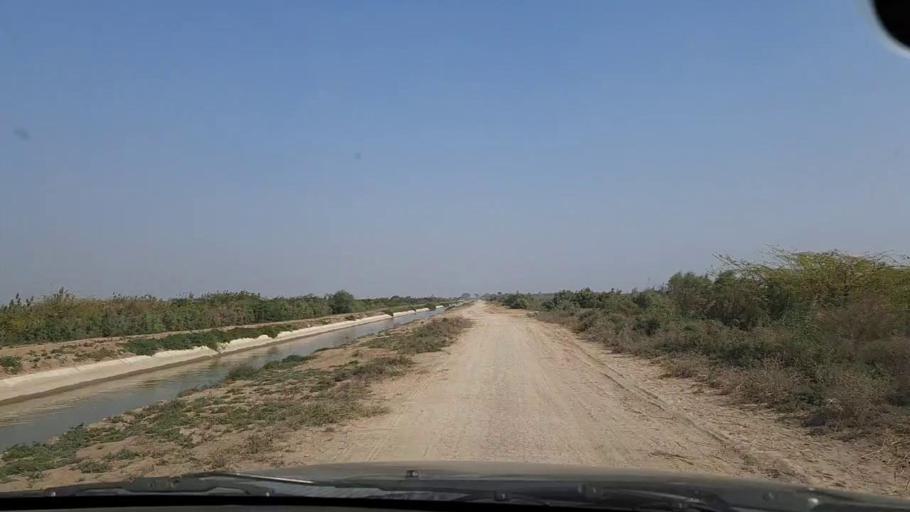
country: PK
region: Sindh
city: Mirpur Sakro
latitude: 24.3419
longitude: 67.7173
